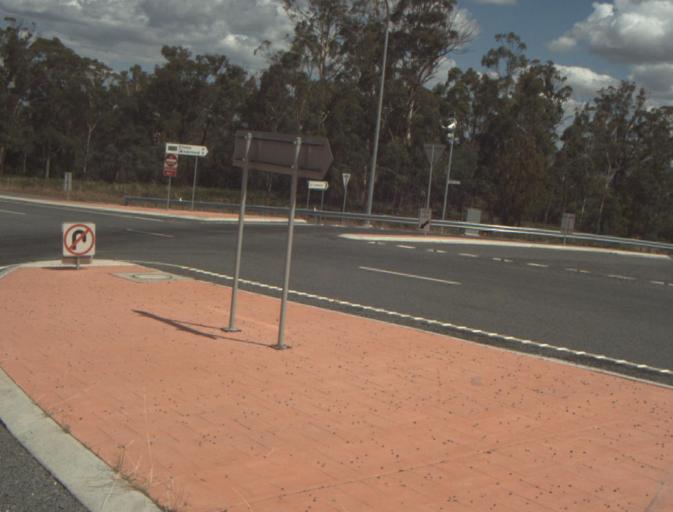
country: AU
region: Tasmania
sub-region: Launceston
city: Mayfield
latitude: -41.3018
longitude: 147.0505
